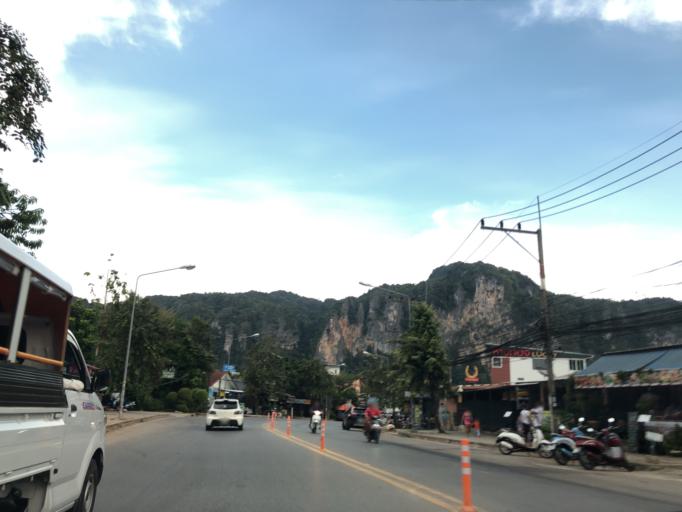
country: TH
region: Phangnga
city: Ban Ao Nang
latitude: 8.0383
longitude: 98.8333
